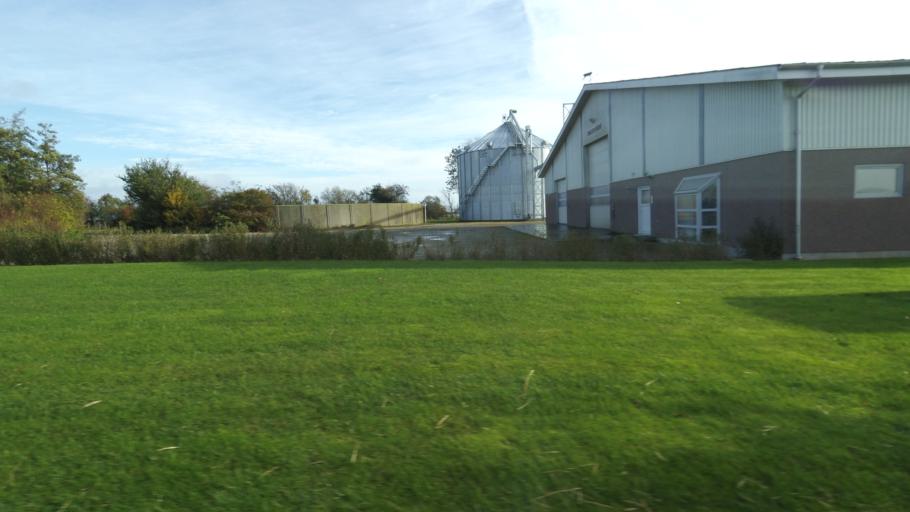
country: DK
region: Central Jutland
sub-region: Odder Kommune
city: Odder
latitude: 55.9358
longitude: 10.2357
